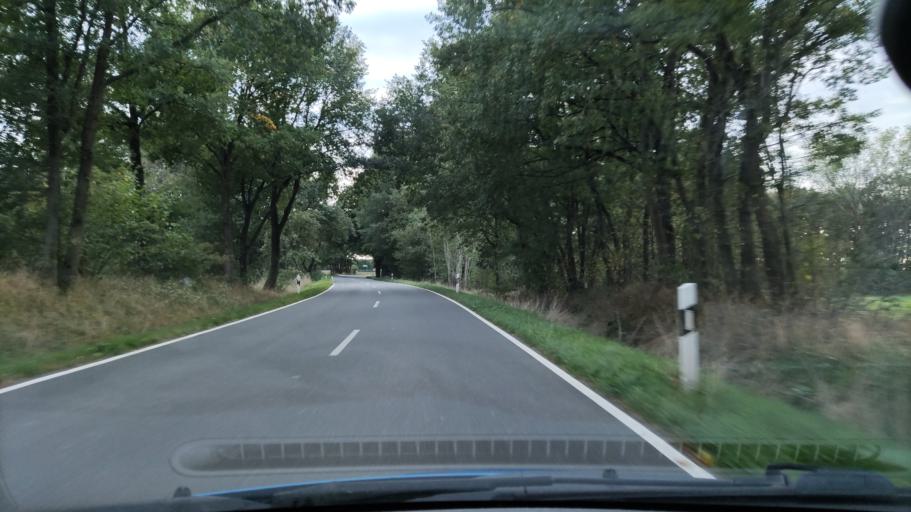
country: DE
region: Mecklenburg-Vorpommern
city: Boizenburg
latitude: 53.4106
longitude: 10.8362
